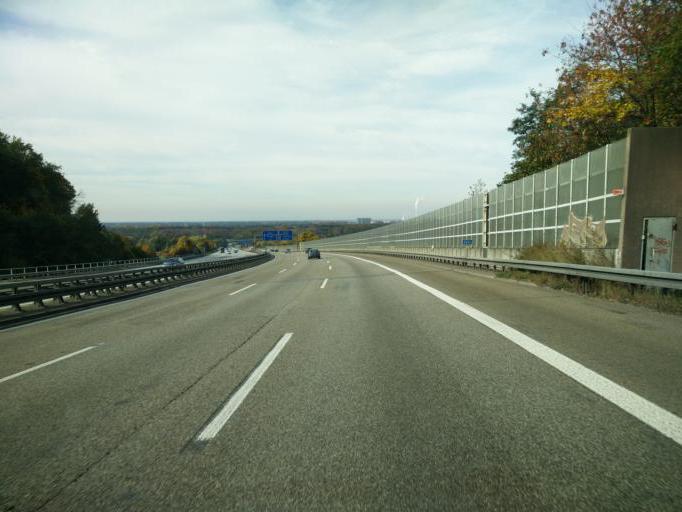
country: DE
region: Baden-Wuerttemberg
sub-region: Karlsruhe Region
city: Ettlingen
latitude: 48.9714
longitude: 8.4563
